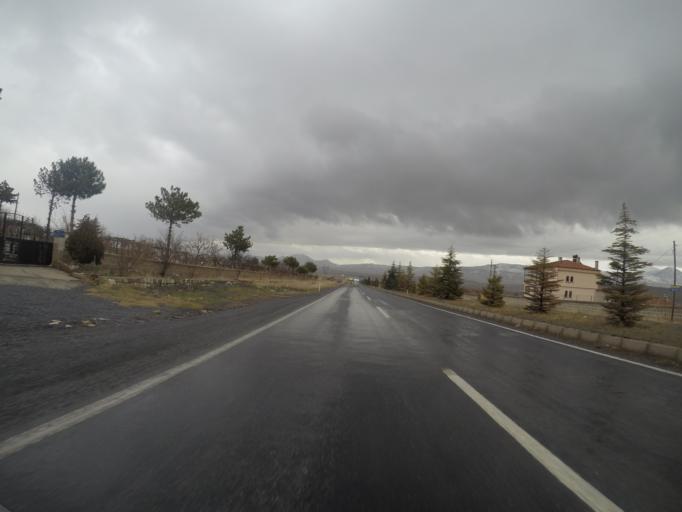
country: TR
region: Kayseri
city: Incesu
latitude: 38.6810
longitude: 35.2226
